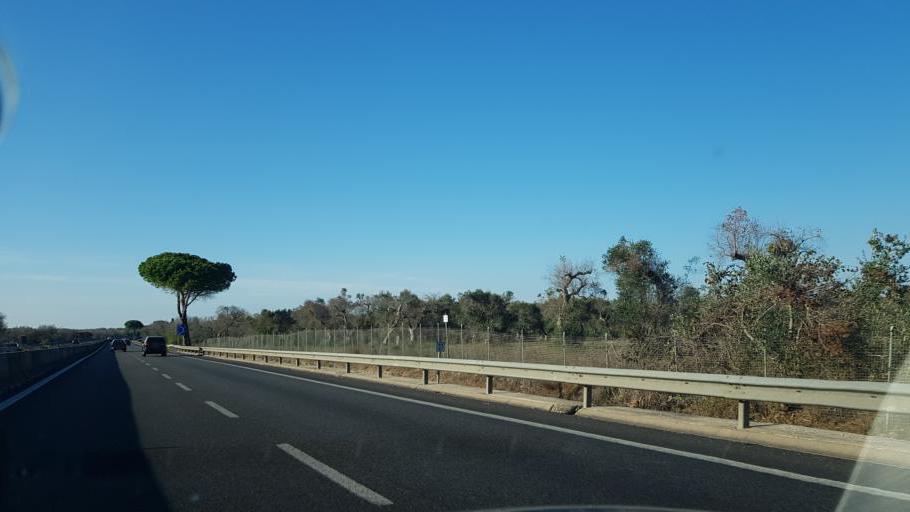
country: IT
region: Apulia
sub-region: Provincia di Lecce
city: Squinzano
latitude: 40.4504
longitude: 18.0685
